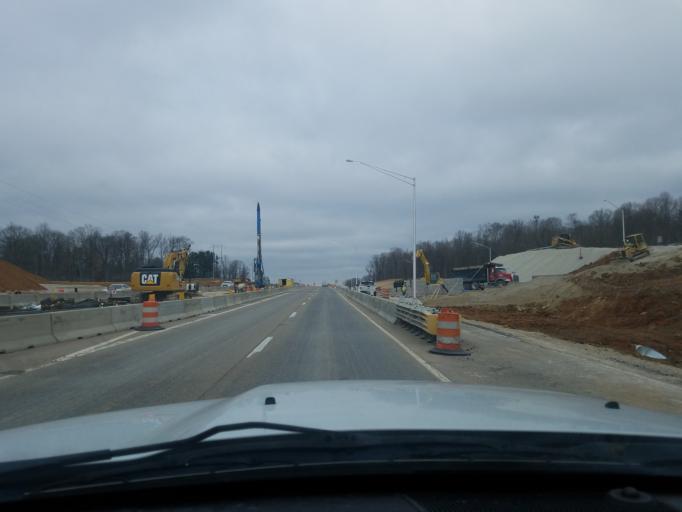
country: US
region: Indiana
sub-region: Monroe County
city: Bloomington
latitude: 39.1360
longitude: -86.5729
